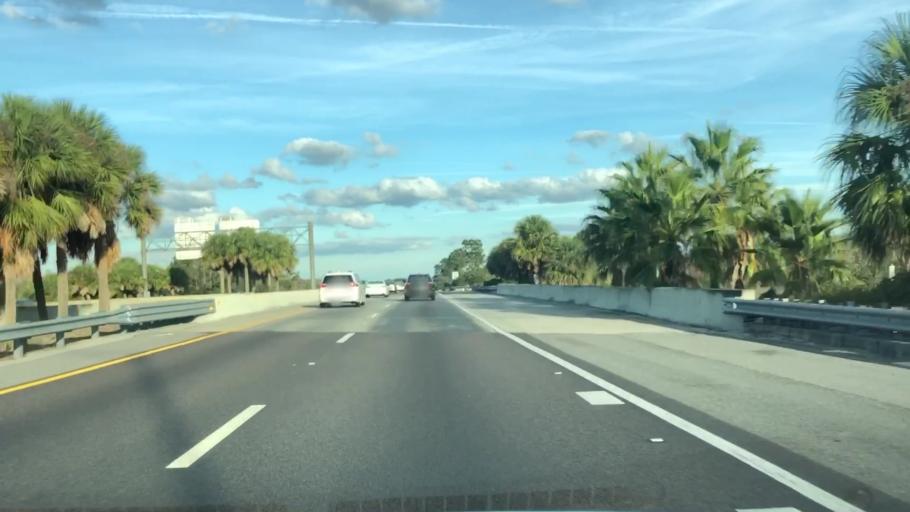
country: US
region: Florida
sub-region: Orange County
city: Hunters Creek
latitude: 28.3569
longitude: -81.4526
